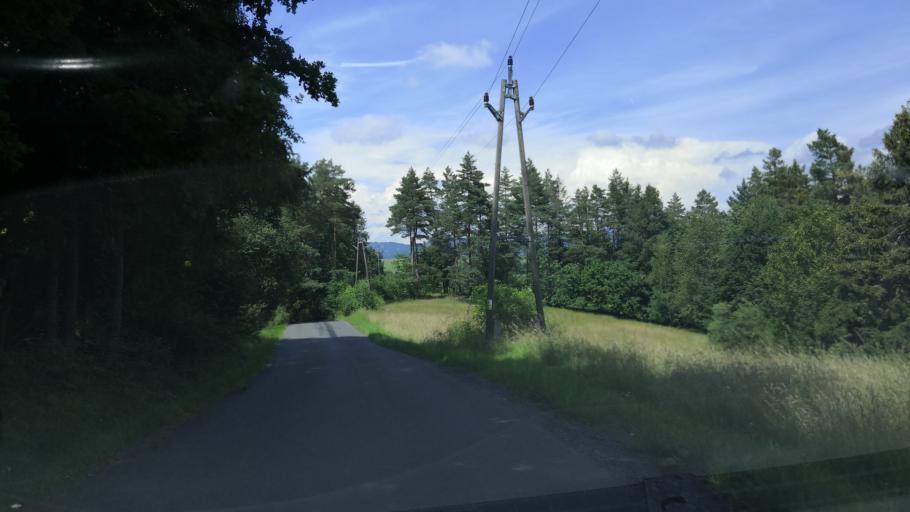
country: CZ
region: Zlin
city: Vidce
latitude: 49.4347
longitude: 18.0942
